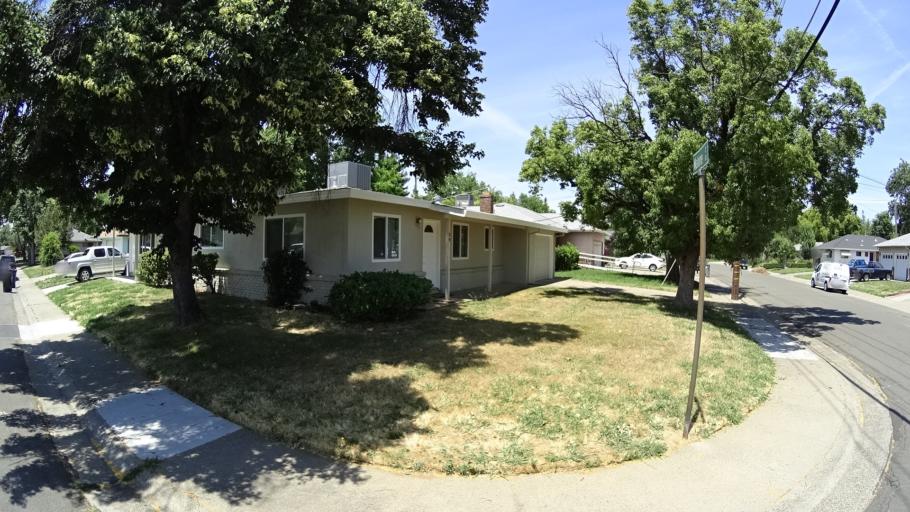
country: US
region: California
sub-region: Sacramento County
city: Florin
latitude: 38.5332
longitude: -121.4224
